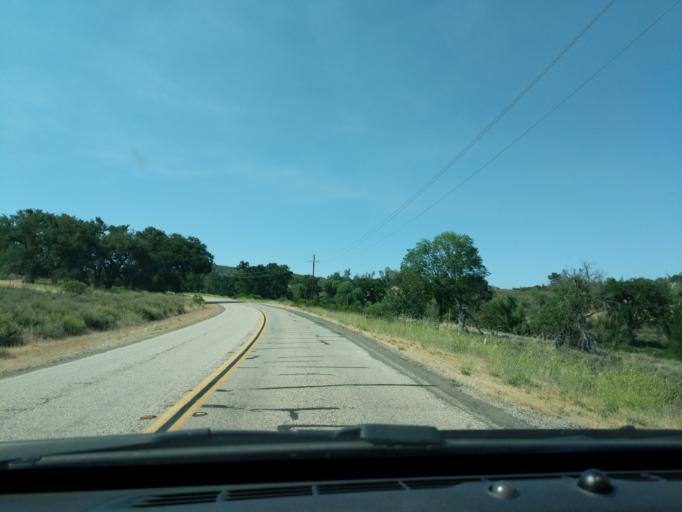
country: US
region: California
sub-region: Monterey County
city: King City
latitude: 35.9726
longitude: -121.1755
